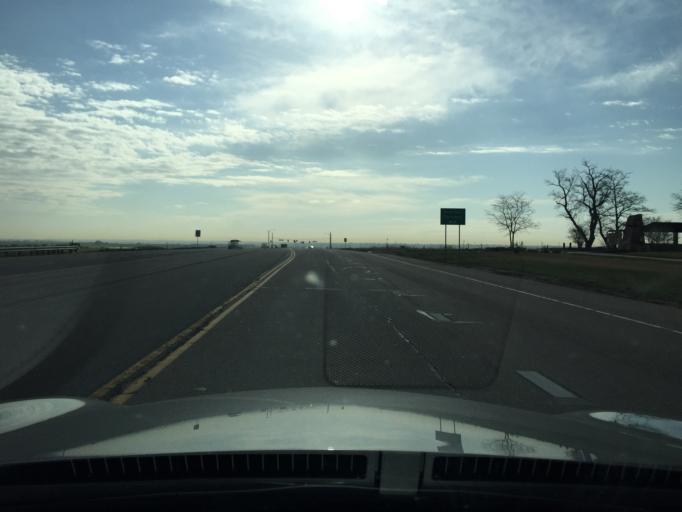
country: US
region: Colorado
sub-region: Boulder County
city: Erie
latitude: 40.0003
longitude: -105.0122
